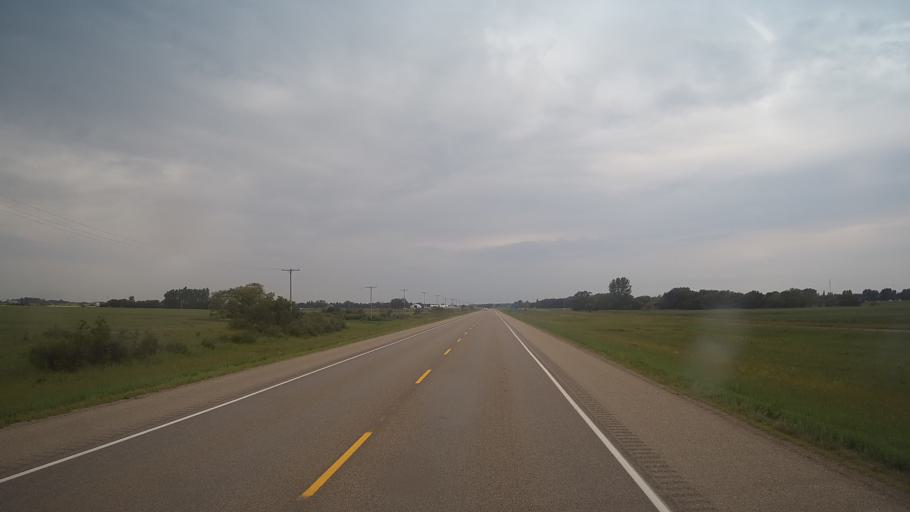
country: CA
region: Saskatchewan
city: Langham
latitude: 52.1289
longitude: -107.2075
